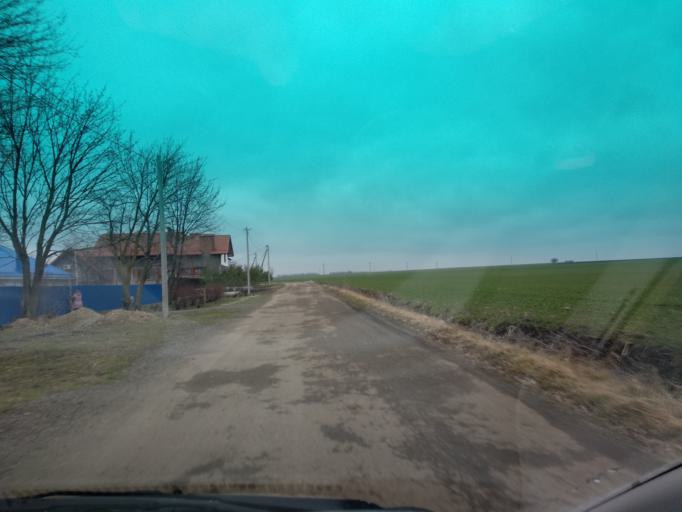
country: RU
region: Krasnodarskiy
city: Vyselki
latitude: 45.6628
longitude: 39.7025
